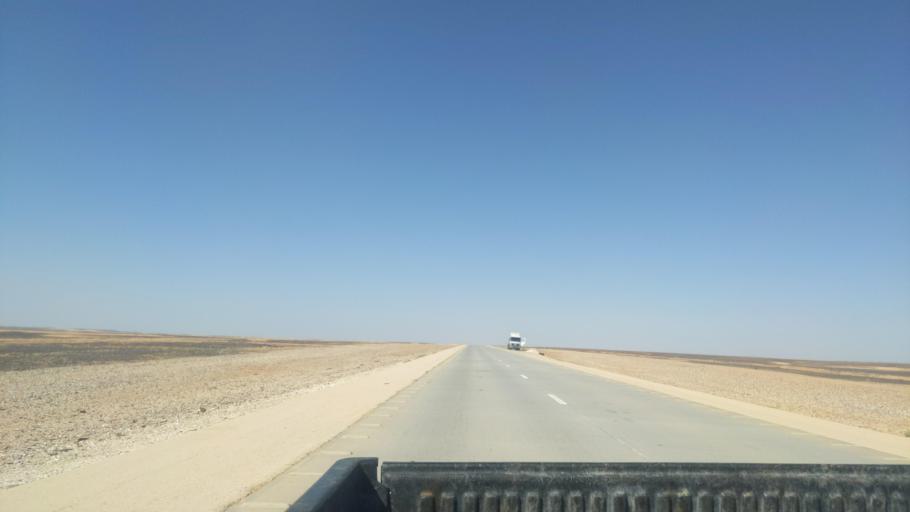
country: JO
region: Amman
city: Al Azraq ash Shamali
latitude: 31.4297
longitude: 36.7356
